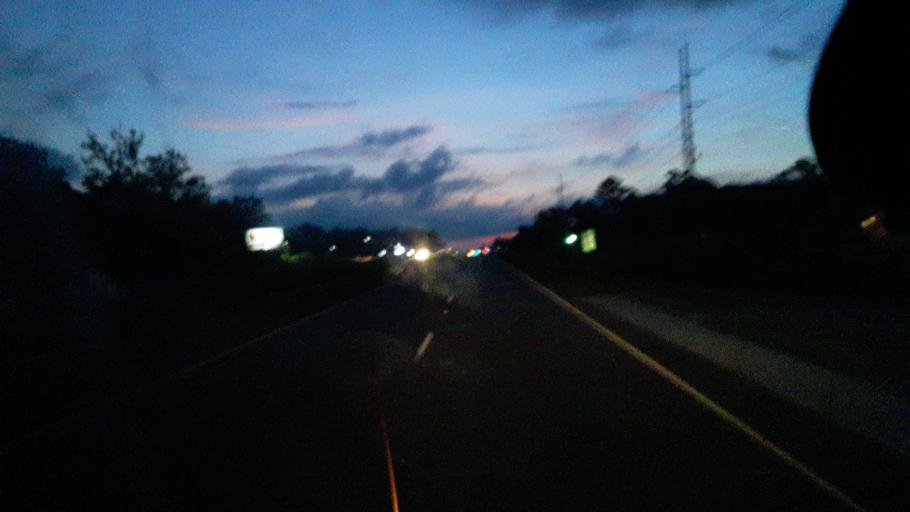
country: US
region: North Carolina
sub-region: Brunswick County
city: Shallotte
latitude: 34.0127
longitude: -78.2856
